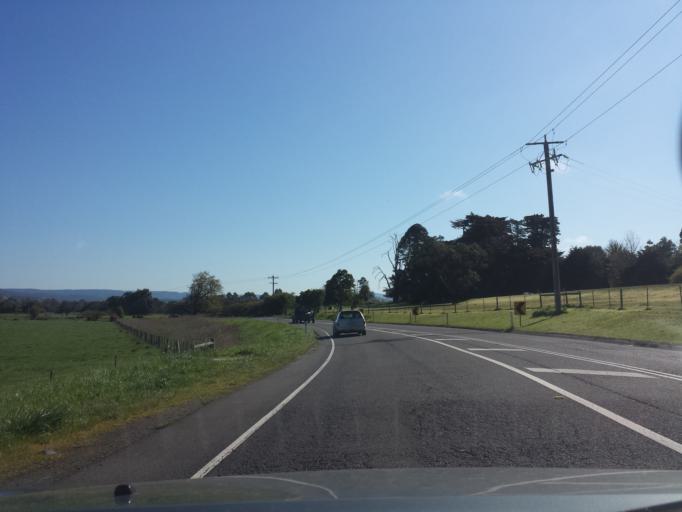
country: AU
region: Victoria
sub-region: Yarra Ranges
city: Yarra Glen
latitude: -37.6734
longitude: 145.3815
